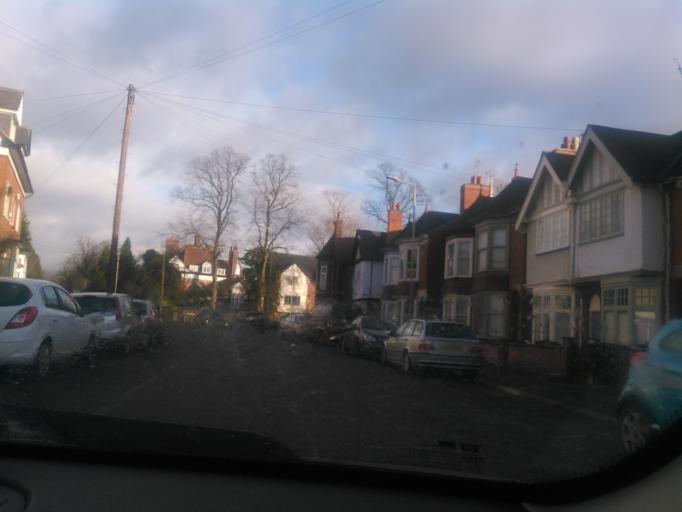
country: GB
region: England
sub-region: Leicestershire
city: Oadby
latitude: 52.6103
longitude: -1.1140
